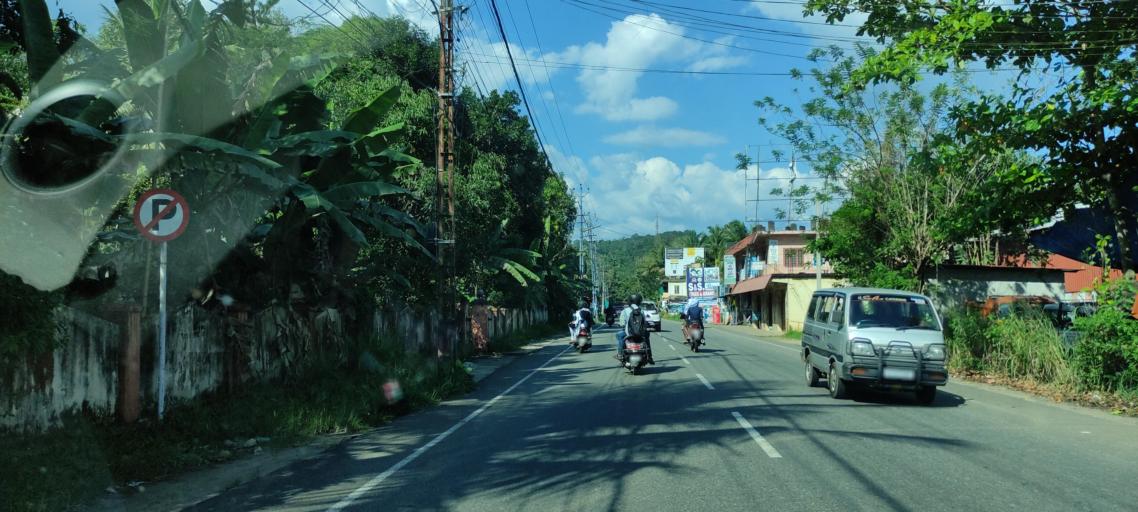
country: IN
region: Kerala
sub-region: Pattanamtitta
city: Pathanamthitta
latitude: 9.2472
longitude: 76.7572
